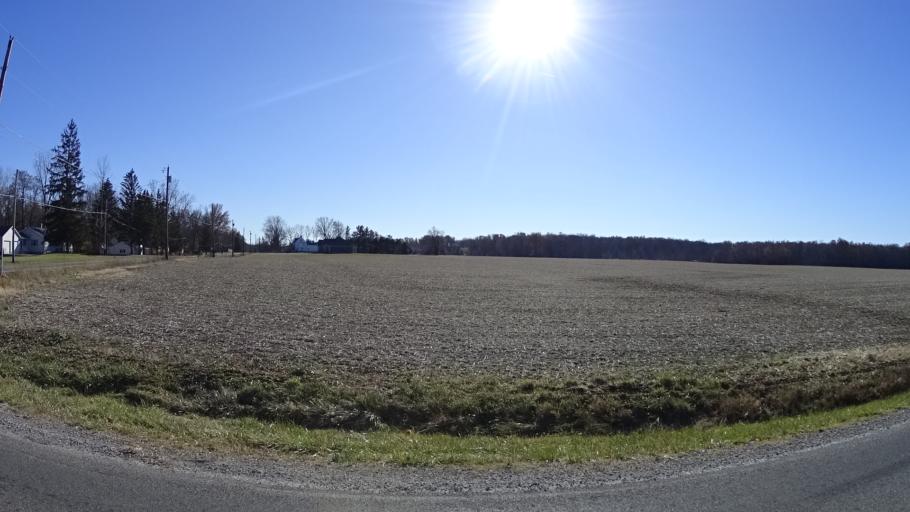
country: US
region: Ohio
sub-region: Lorain County
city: Grafton
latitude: 41.2851
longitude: -82.0819
